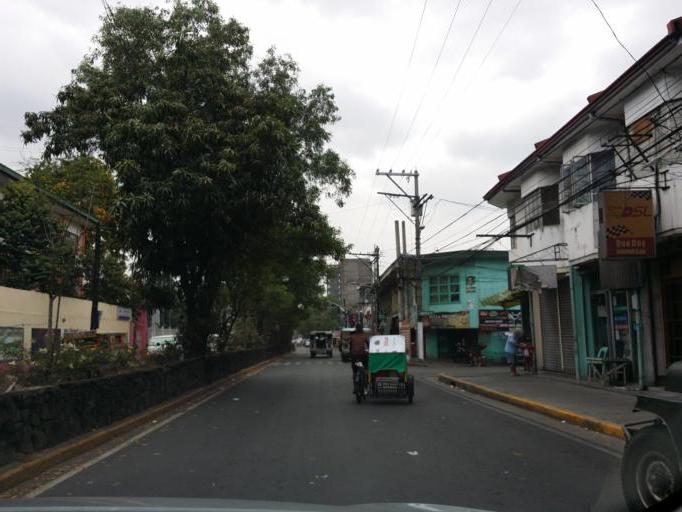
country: PH
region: Metro Manila
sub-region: Makati City
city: Makati City
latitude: 14.5679
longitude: 121.0049
